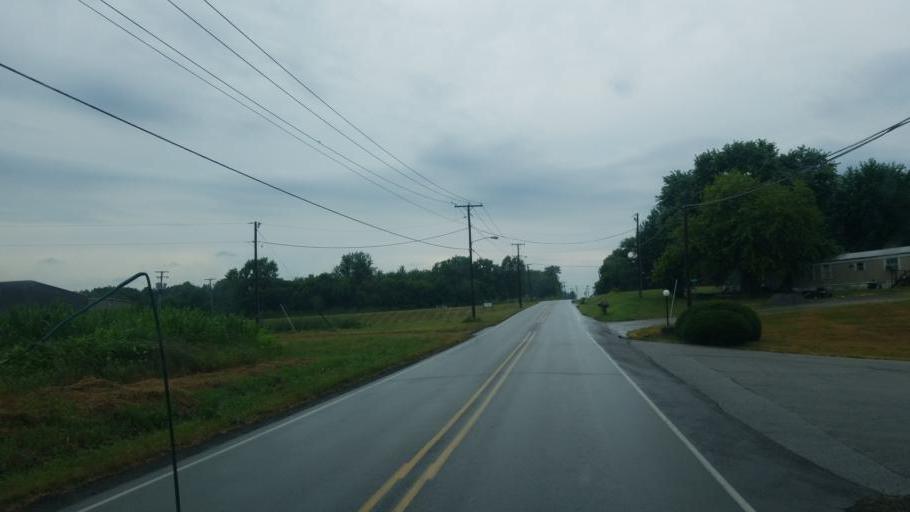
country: US
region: Indiana
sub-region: Steuben County
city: Hamilton
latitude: 41.5368
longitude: -84.9269
